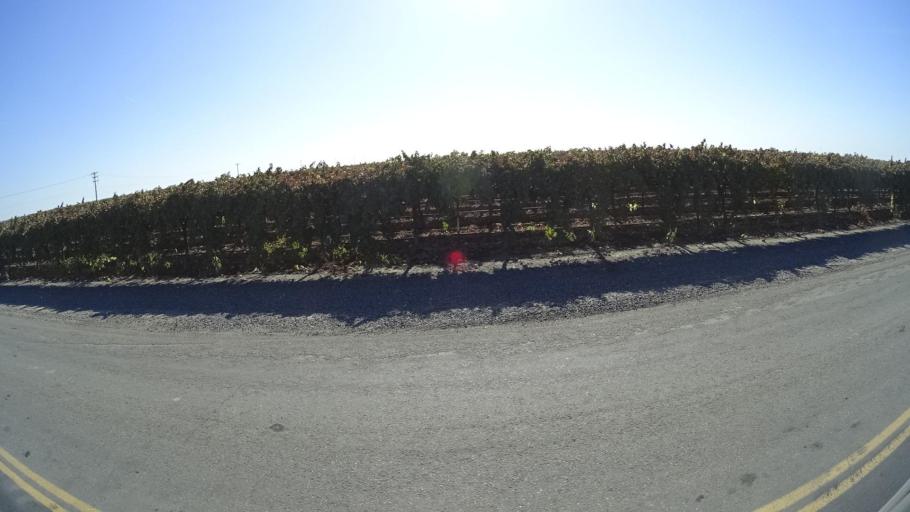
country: US
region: California
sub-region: Kern County
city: McFarland
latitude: 35.7034
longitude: -119.2061
